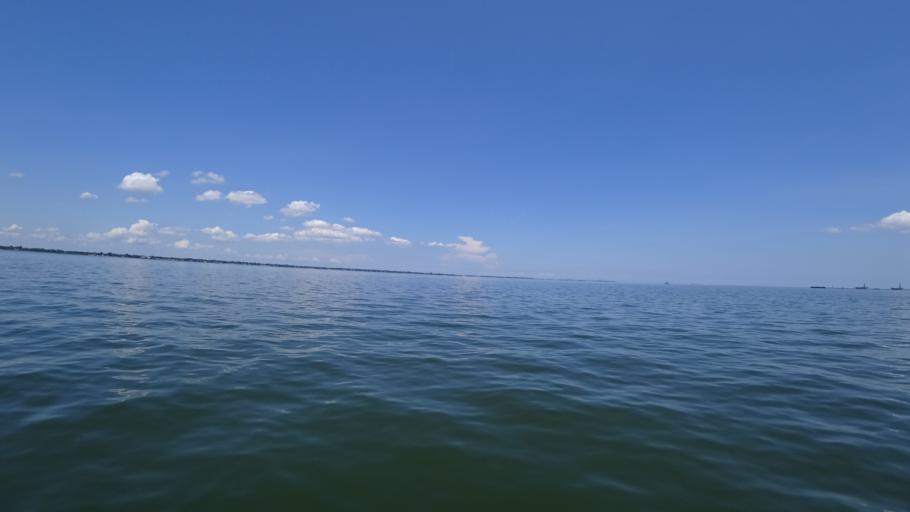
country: US
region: Virginia
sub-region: City of Newport News
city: Newport News
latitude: 36.9571
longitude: -76.3833
